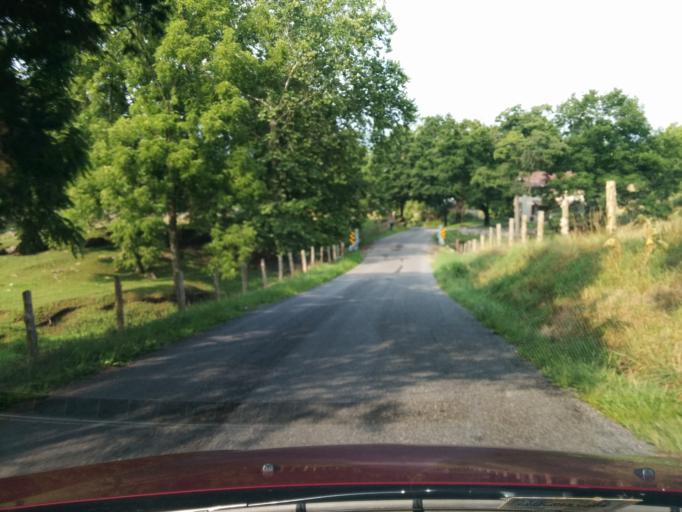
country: US
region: Virginia
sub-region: City of Lexington
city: Lexington
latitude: 37.7527
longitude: -79.5123
